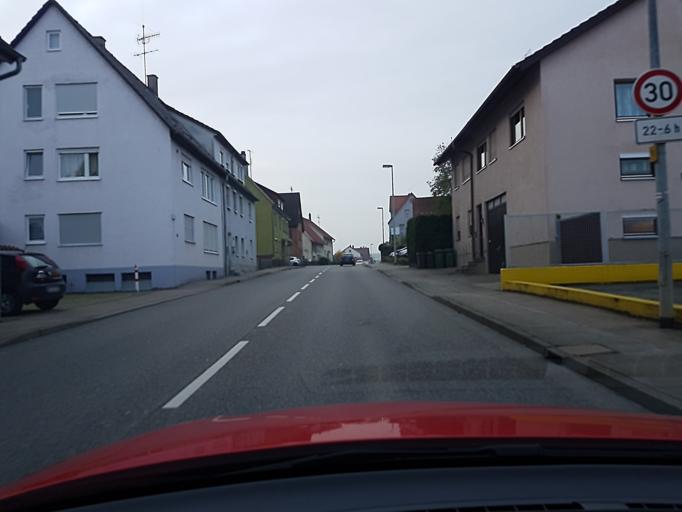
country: DE
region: Baden-Wuerttemberg
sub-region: Regierungsbezirk Stuttgart
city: Kirchheim am Neckar
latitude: 49.0418
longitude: 9.1439
